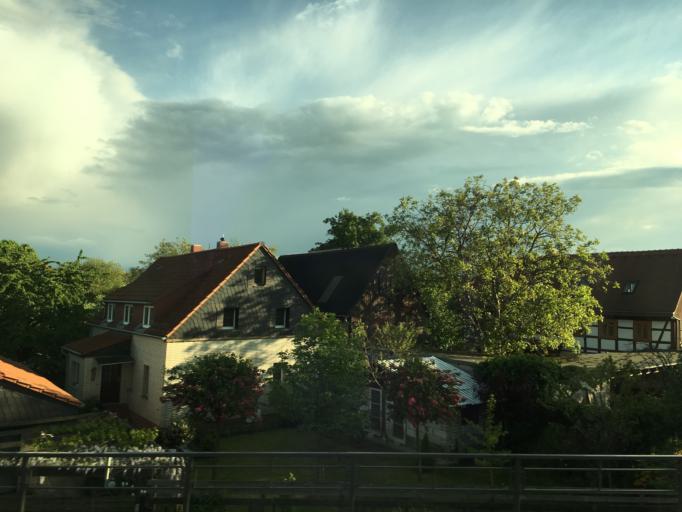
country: DE
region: Saxony
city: Dresden
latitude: 51.0879
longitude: 13.7118
